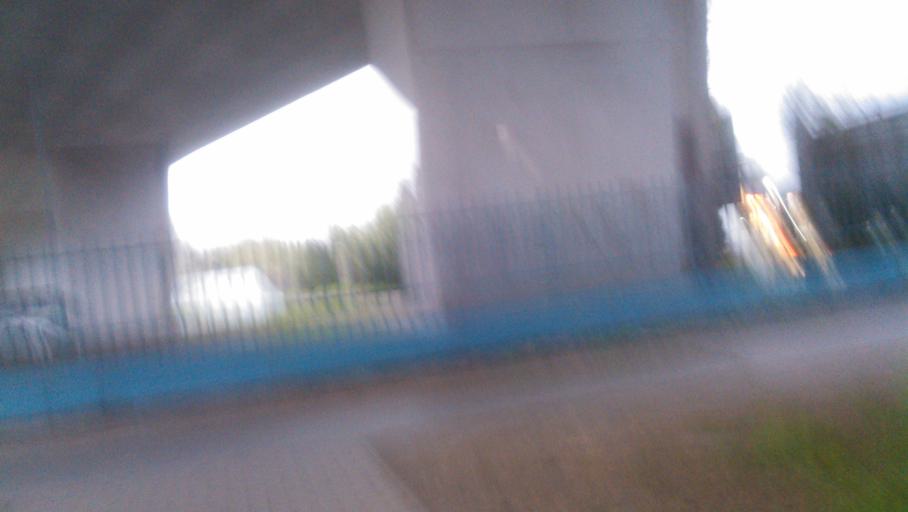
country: SK
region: Presovsky
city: Humenne
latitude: 48.9316
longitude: 21.9095
